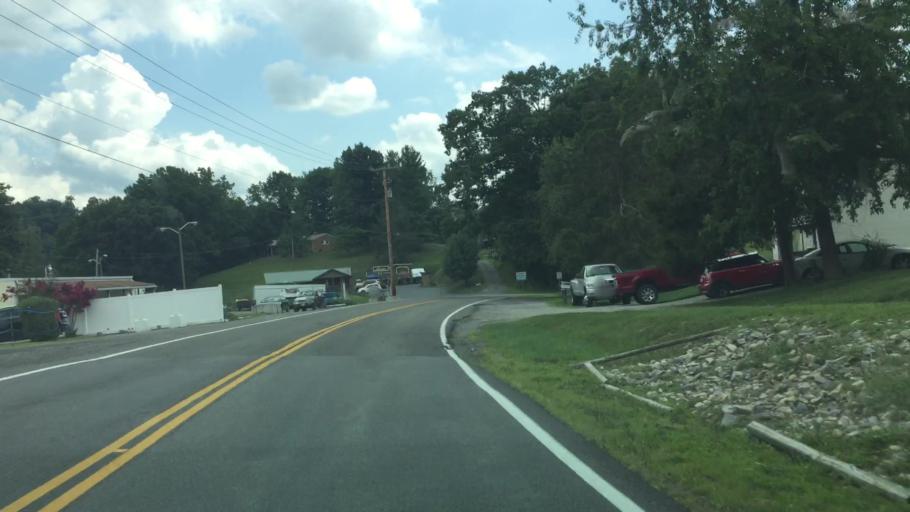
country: US
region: Virginia
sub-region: Pulaski County
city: Dublin
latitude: 37.0471
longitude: -80.7109
